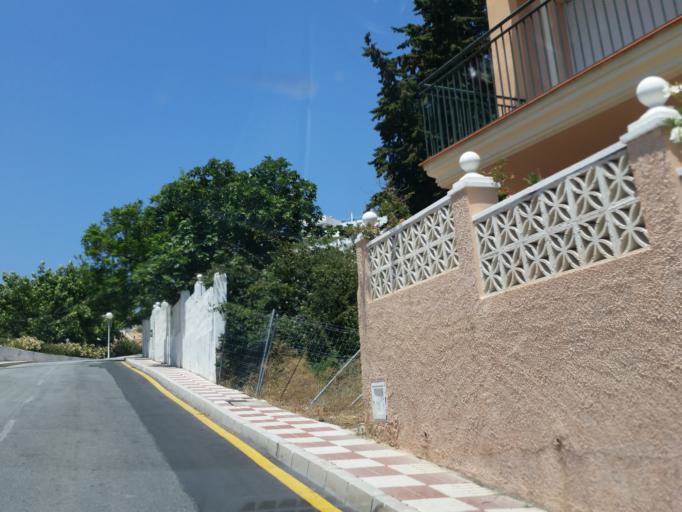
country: ES
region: Andalusia
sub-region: Provincia de Malaga
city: Fuengirola
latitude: 36.5648
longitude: -4.6053
